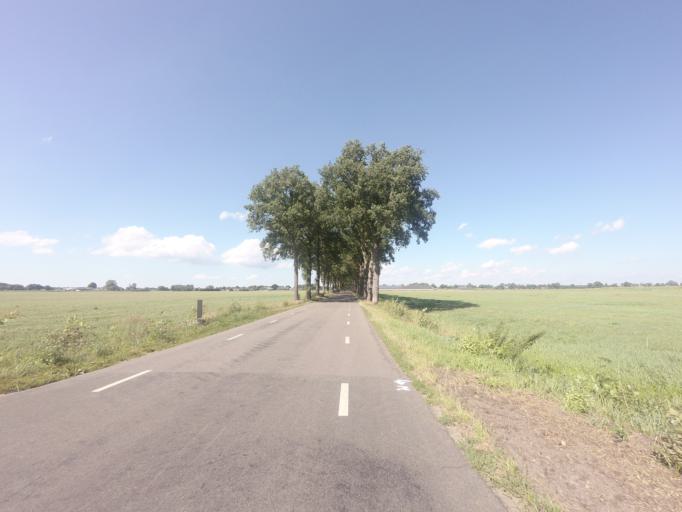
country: NL
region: Overijssel
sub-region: Gemeente Twenterand
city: Den Ham
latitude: 52.5551
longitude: 6.4367
